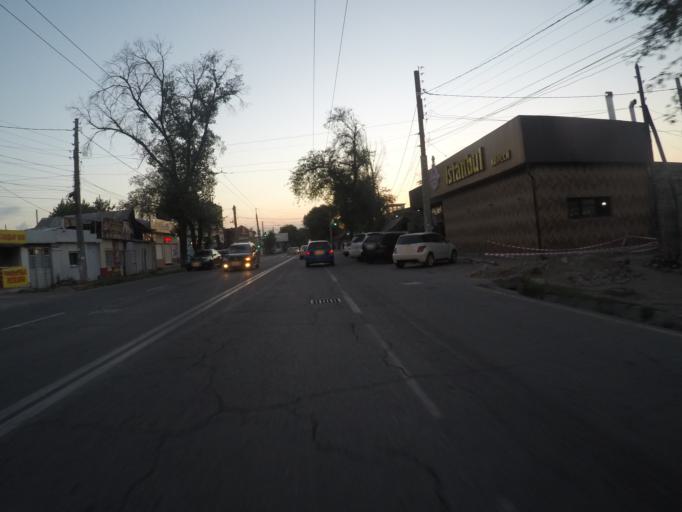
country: KG
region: Chuy
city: Bishkek
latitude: 42.8572
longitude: 74.6007
